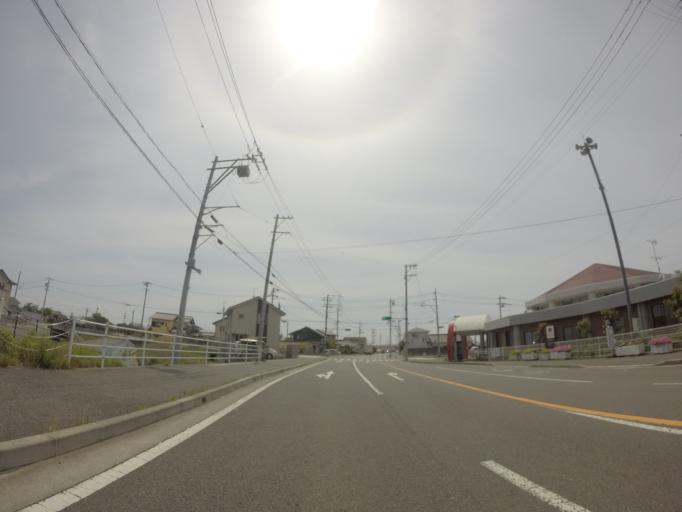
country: JP
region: Shizuoka
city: Fujieda
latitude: 34.8079
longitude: 138.2876
